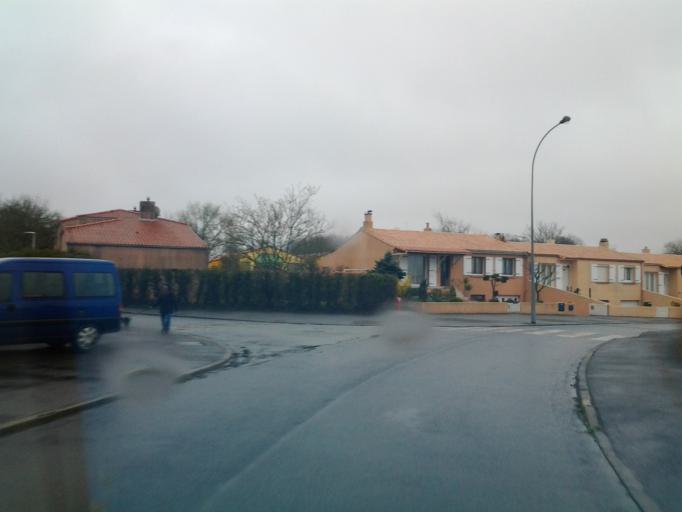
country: FR
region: Pays de la Loire
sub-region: Departement de la Vendee
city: La Roche-sur-Yon
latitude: 46.6671
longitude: -1.4567
